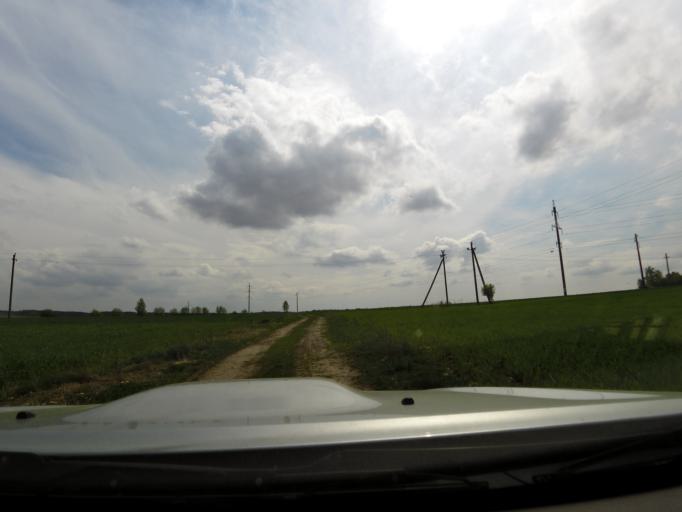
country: LT
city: Salcininkai
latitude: 54.4184
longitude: 25.3109
